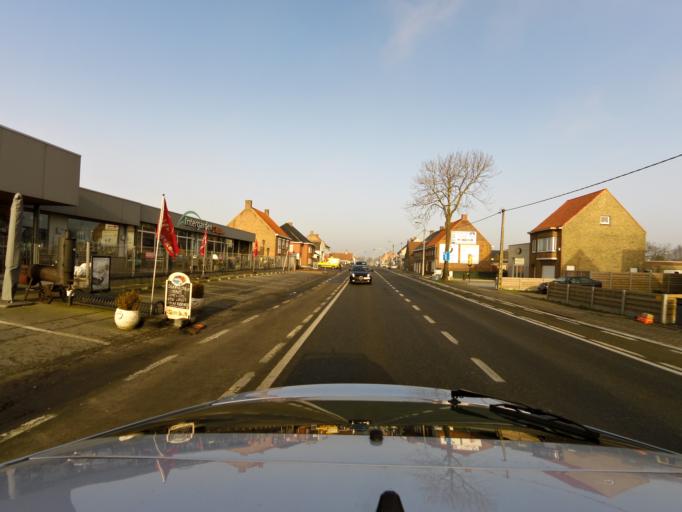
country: BE
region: Flanders
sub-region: Provincie West-Vlaanderen
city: Ichtegem
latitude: 51.1005
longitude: 3.0333
